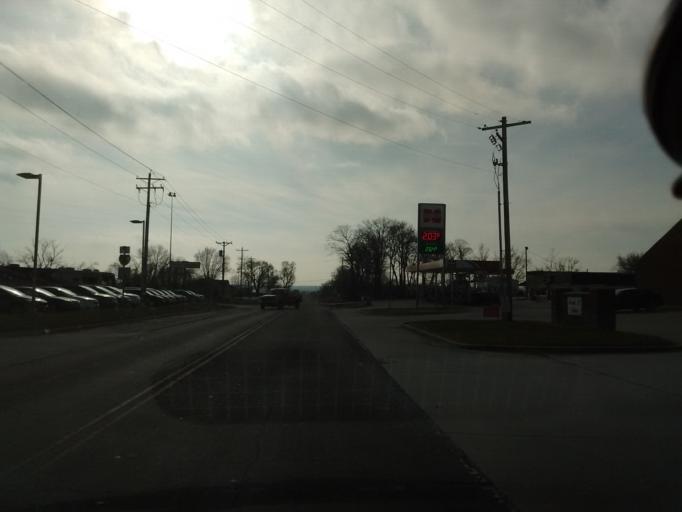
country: US
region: Missouri
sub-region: Cooper County
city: Boonville
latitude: 38.9345
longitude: -92.7436
